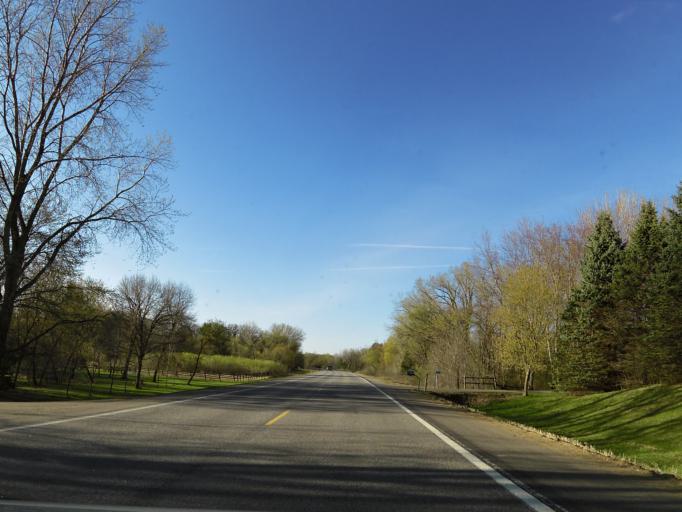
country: US
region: Minnesota
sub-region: Scott County
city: Elko New Market
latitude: 44.5757
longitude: -93.2846
